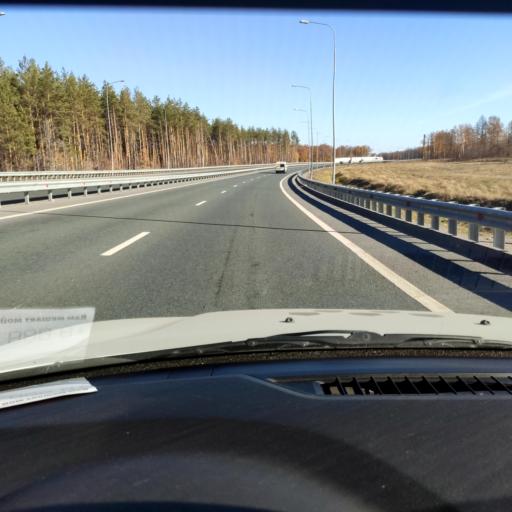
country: RU
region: Samara
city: Bereza
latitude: 53.5048
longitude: 50.1211
